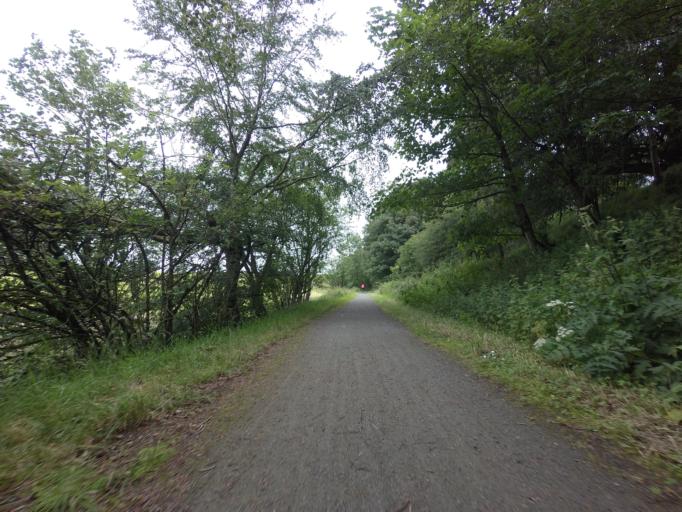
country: GB
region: Scotland
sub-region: Aberdeenshire
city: Mintlaw
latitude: 57.5103
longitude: -2.1415
